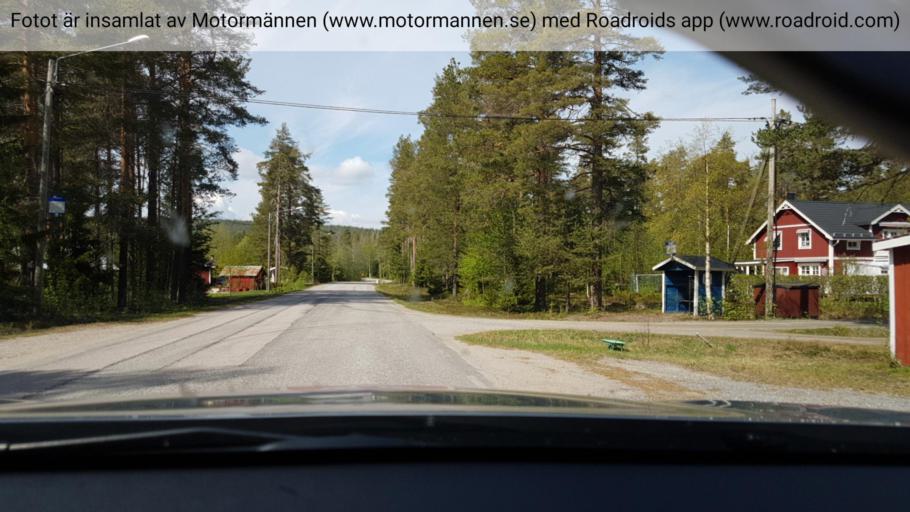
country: SE
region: Vaesterbotten
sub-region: Umea Kommun
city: Roback
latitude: 63.8375
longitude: 20.0993
